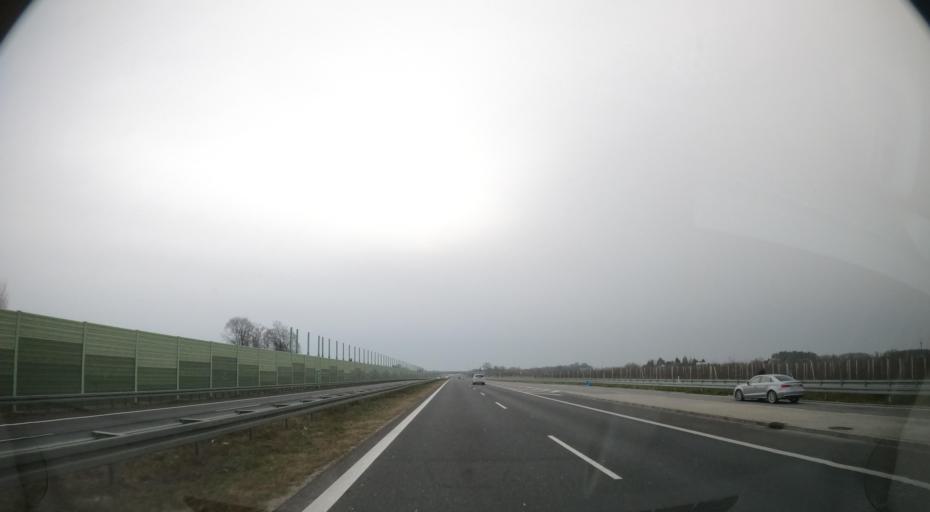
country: PL
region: Masovian Voivodeship
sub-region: Powiat grojecki
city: Jasieniec
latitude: 51.8022
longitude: 20.8884
